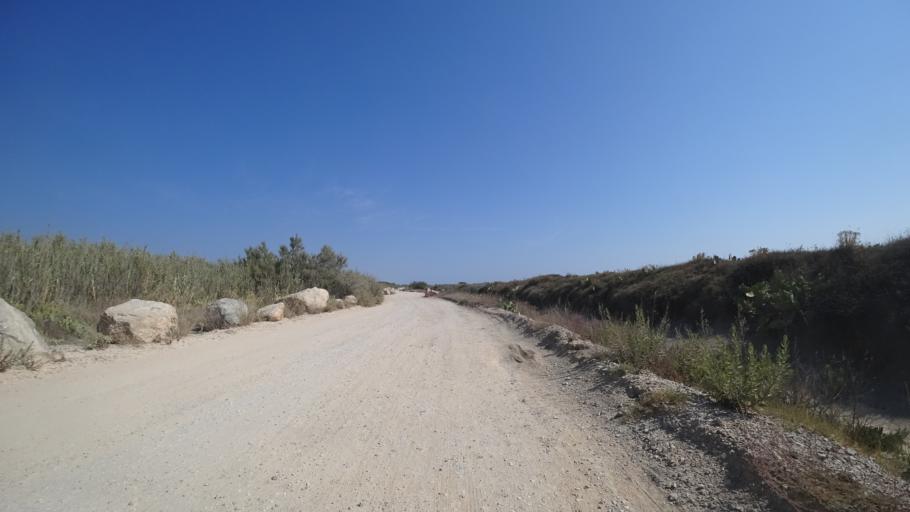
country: FR
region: Languedoc-Roussillon
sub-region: Departement des Pyrenees-Orientales
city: Le Barcares
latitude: 42.7744
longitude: 3.0365
